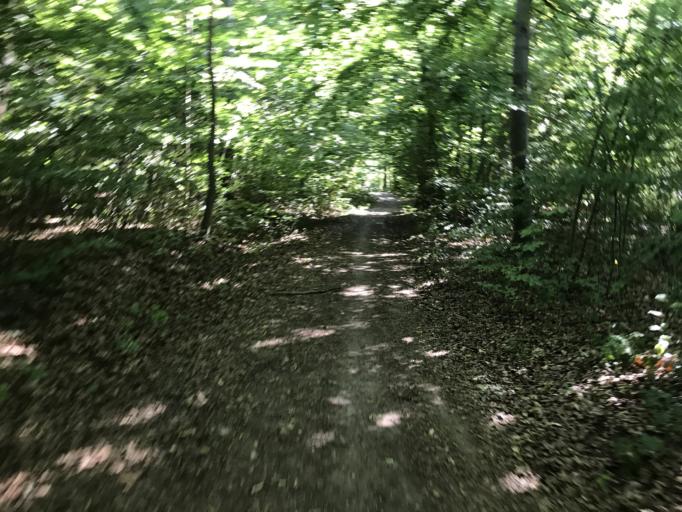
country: DE
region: Baden-Wuerttemberg
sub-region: Regierungsbezirk Stuttgart
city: Stuttgart
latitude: 48.7606
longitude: 9.1844
